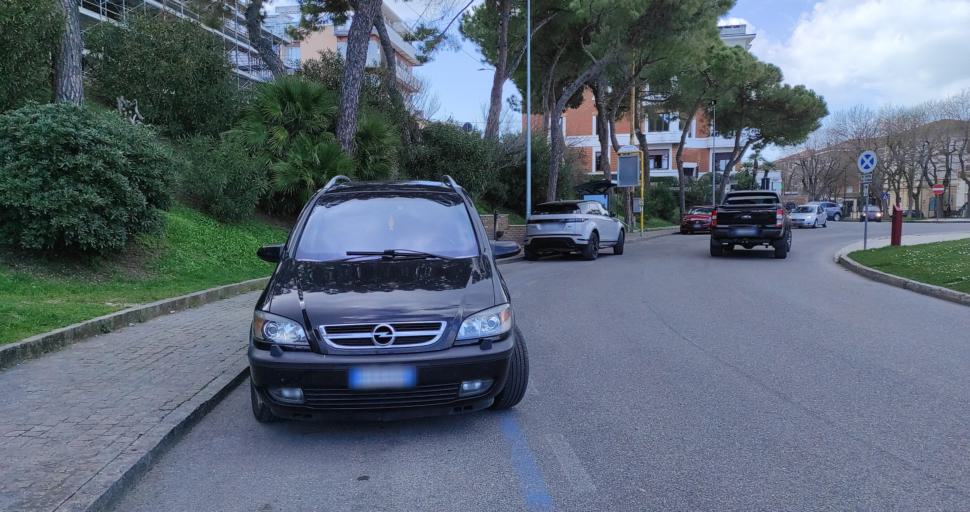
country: IT
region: The Marches
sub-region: Provincia di Ancona
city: Pietra la Croce
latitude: 43.6146
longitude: 13.5337
